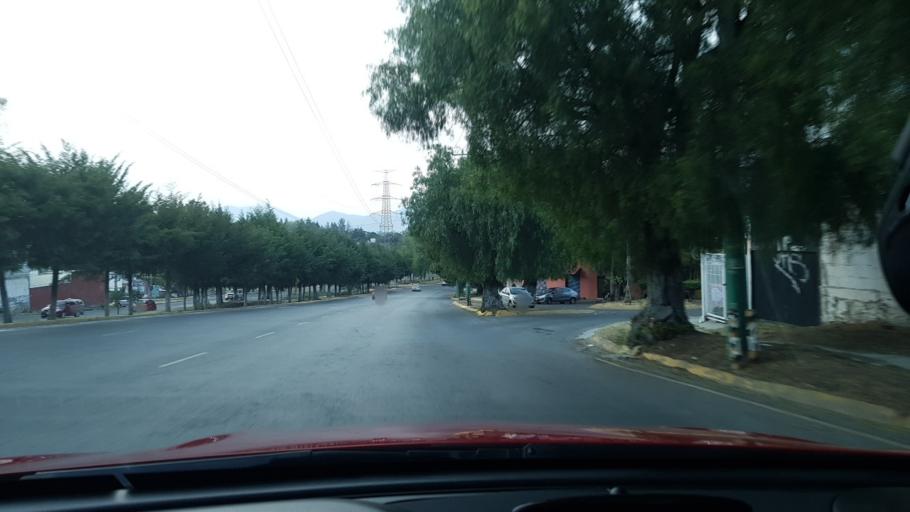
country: MX
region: Mexico
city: Cuautitlan Izcalli
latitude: 19.6431
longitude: -99.2243
